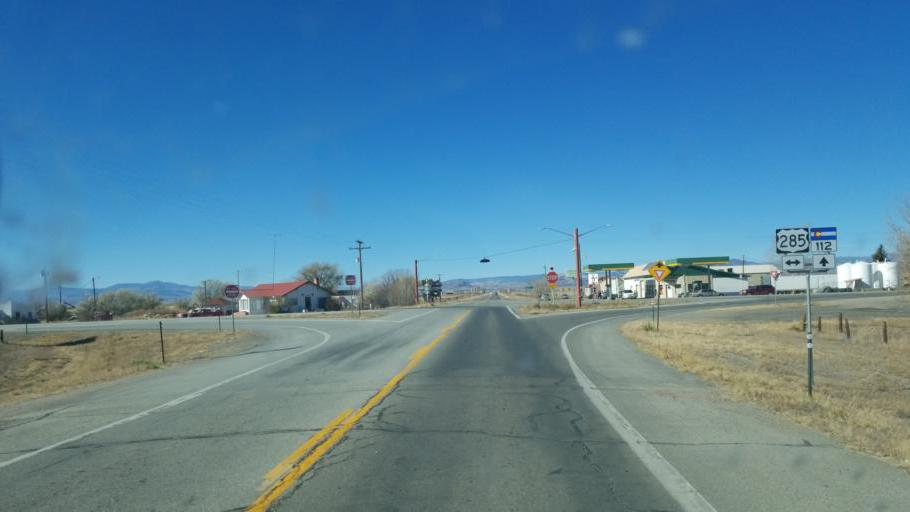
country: US
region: Colorado
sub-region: Saguache County
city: Center
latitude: 37.7482
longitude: -106.1480
